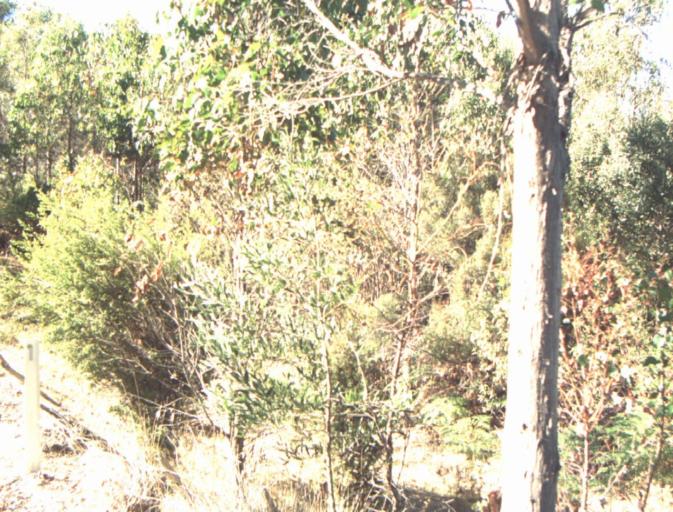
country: AU
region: Tasmania
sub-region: Dorset
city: Scottsdale
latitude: -41.3001
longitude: 147.3554
